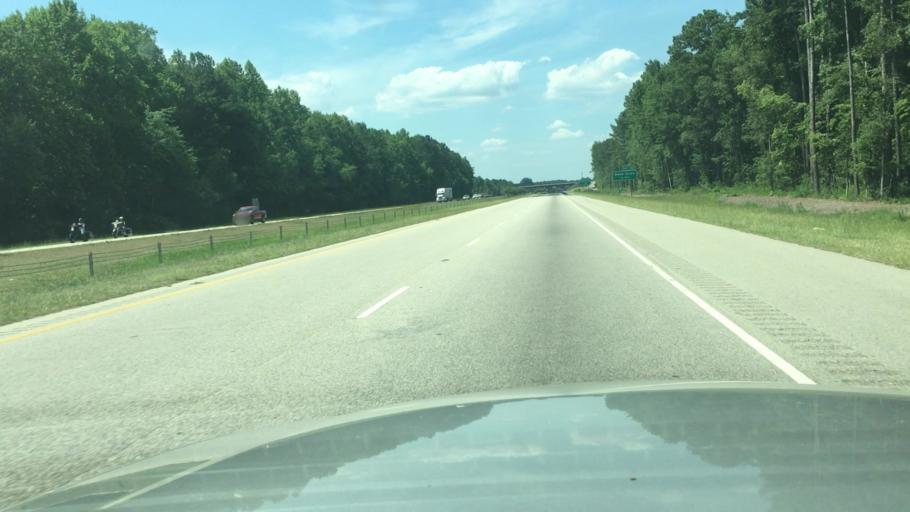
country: US
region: North Carolina
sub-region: Cumberland County
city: Fayetteville
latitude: 35.0019
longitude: -78.8653
